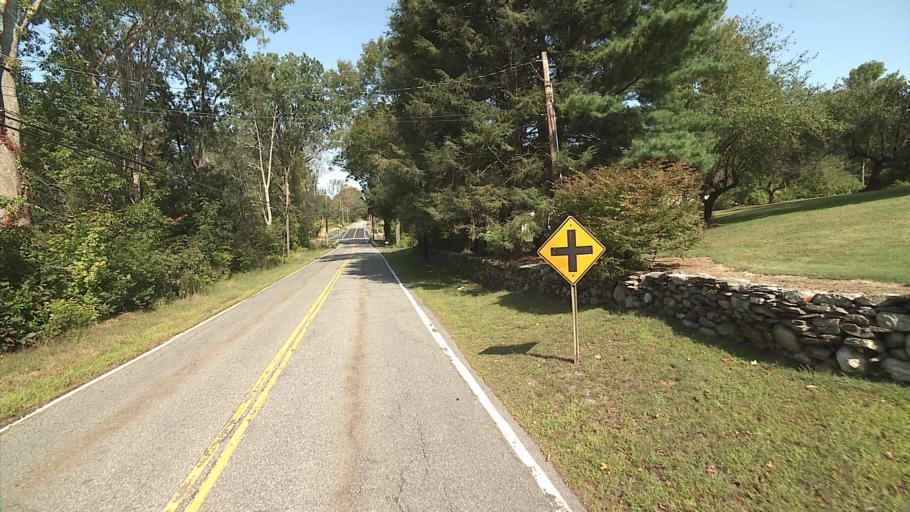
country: US
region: Connecticut
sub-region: Windham County
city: South Woodstock
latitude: 41.9826
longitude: -71.9948
